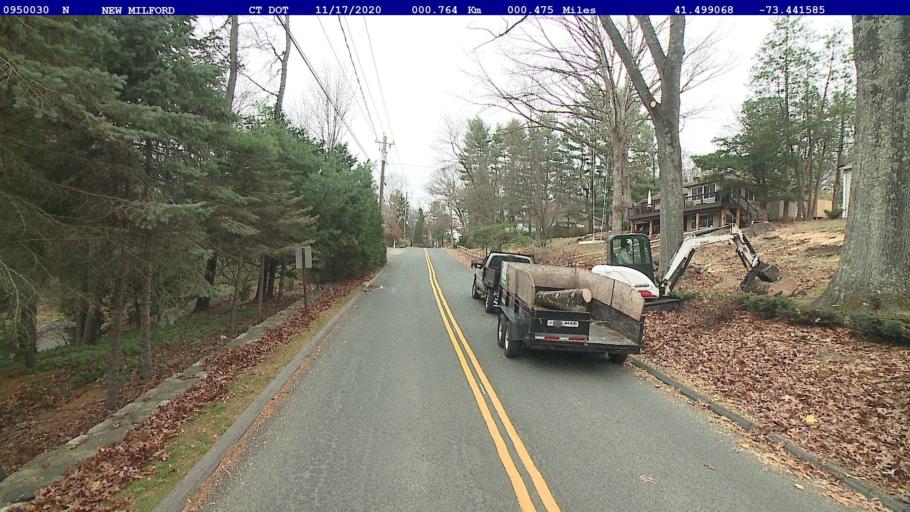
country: US
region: Connecticut
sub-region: Litchfield County
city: New Milford
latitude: 41.4991
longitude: -73.4416
